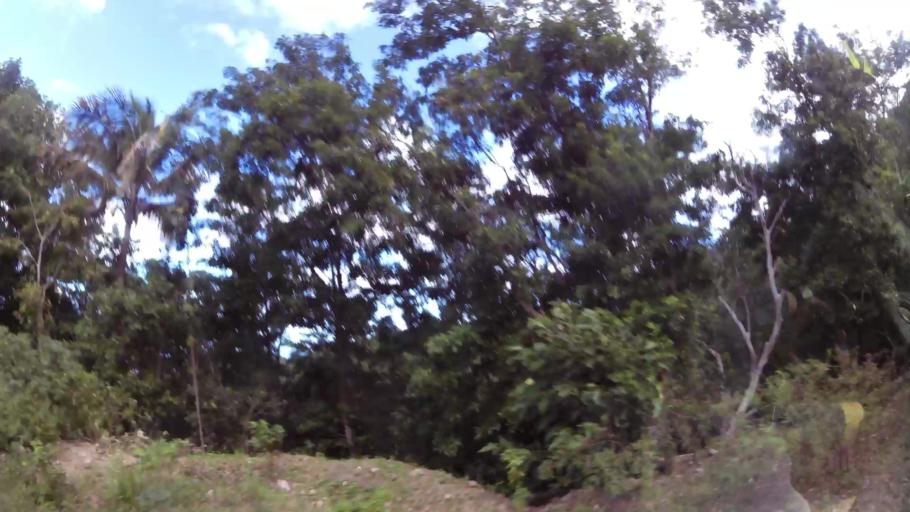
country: DM
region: Saint John
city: Portsmouth
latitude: 15.6352
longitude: -61.4581
